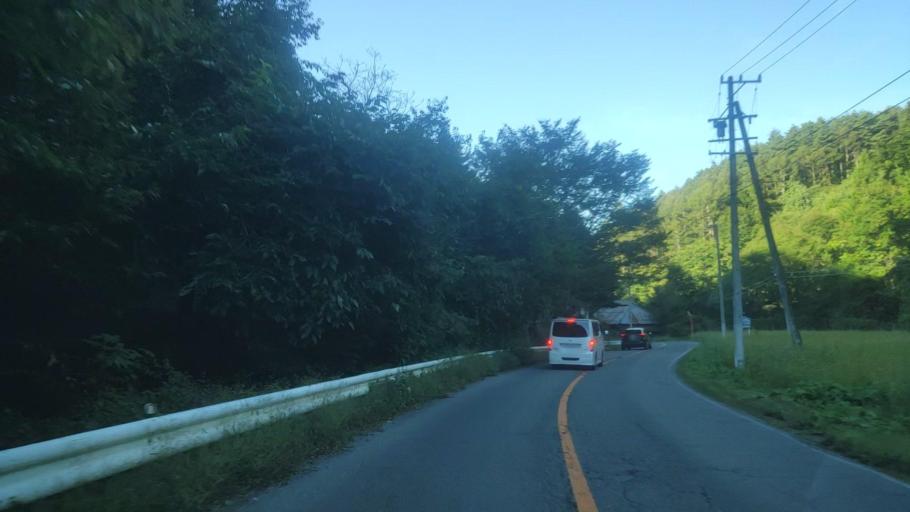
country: JP
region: Nagano
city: Kamimaruko
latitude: 36.2307
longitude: 138.2989
